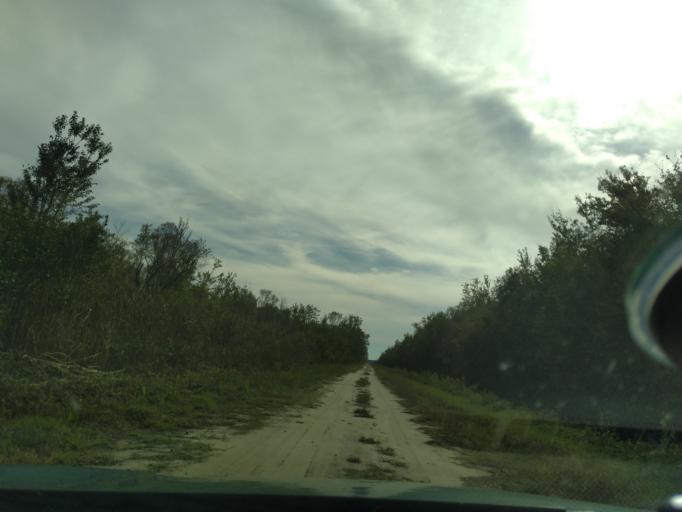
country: US
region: North Carolina
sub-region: Beaufort County
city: Belhaven
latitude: 35.7254
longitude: -76.5725
